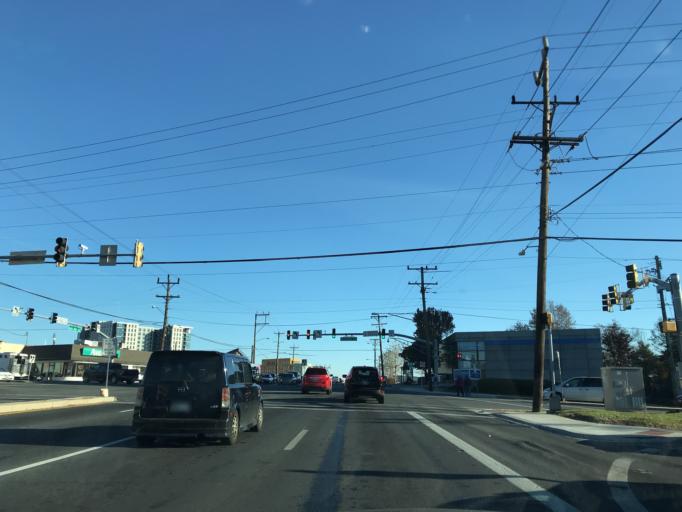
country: US
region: Maryland
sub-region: Montgomery County
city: Wheaton
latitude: 39.0402
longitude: -77.0559
